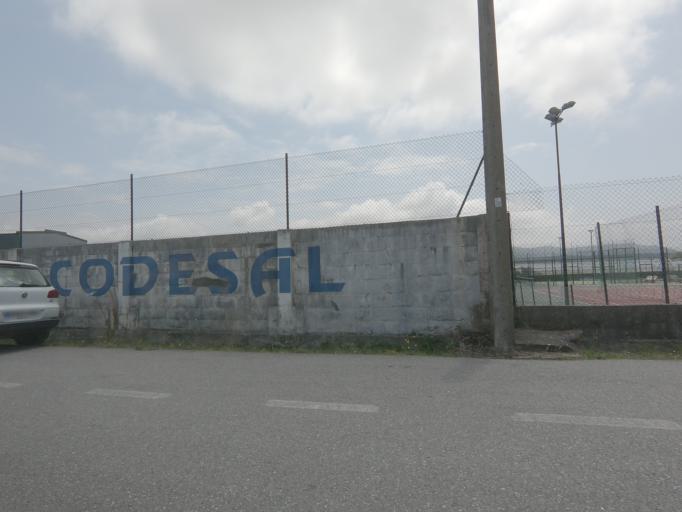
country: ES
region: Galicia
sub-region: Provincia de Pontevedra
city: A Guarda
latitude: 41.8855
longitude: -8.8542
